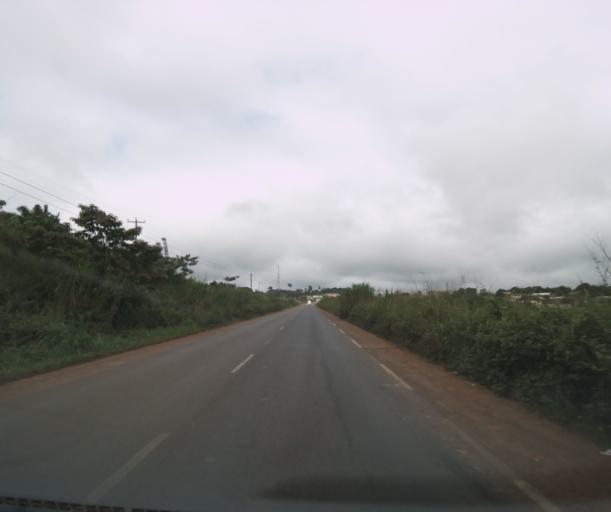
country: CM
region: Centre
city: Mbankomo
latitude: 3.7901
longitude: 11.4085
